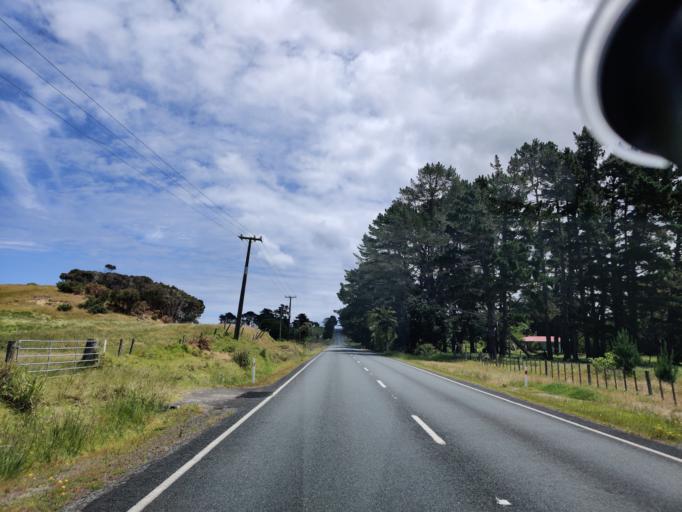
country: NZ
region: Northland
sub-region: Far North District
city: Kaitaia
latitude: -34.6811
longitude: 173.0075
